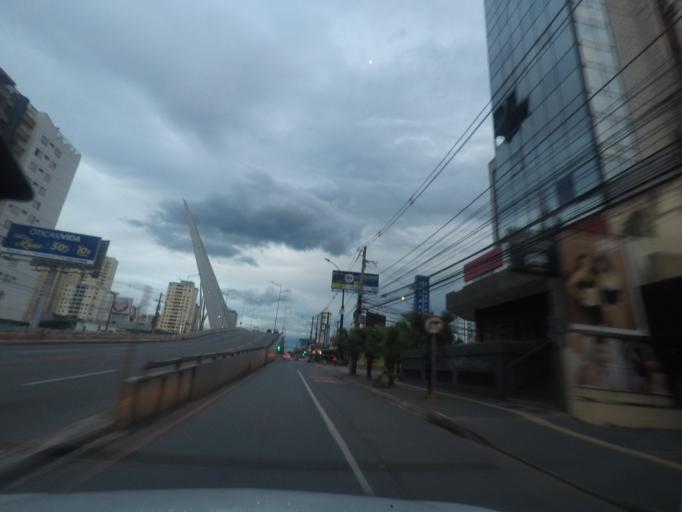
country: BR
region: Goias
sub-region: Goiania
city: Goiania
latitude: -16.7140
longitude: -49.2651
